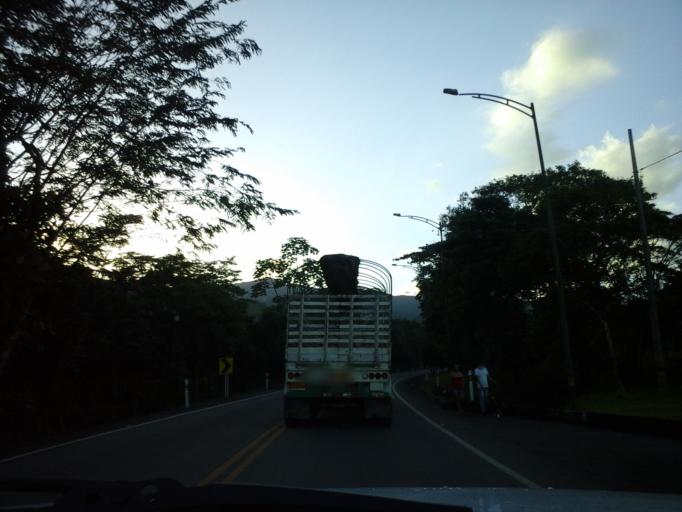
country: CO
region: Meta
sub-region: Villavicencio
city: Villavicencio
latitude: 4.1274
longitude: -73.6526
